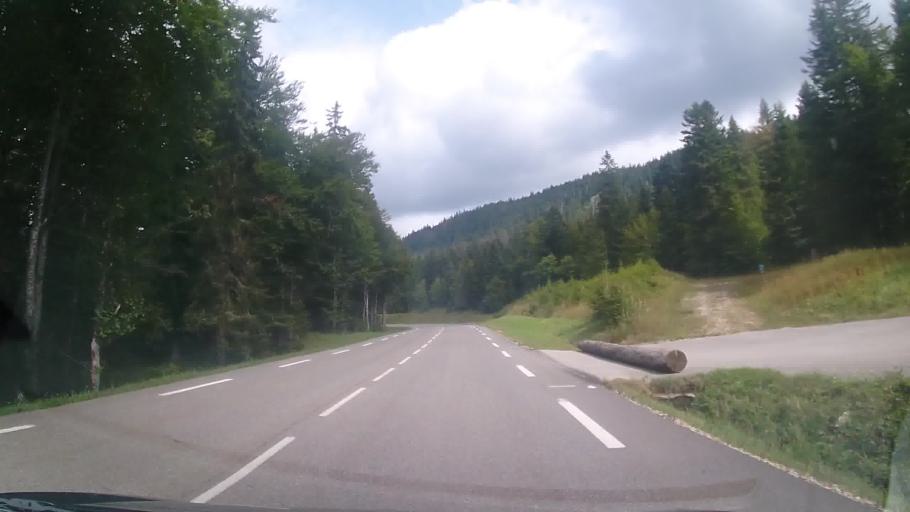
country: FR
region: Rhone-Alpes
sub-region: Departement de l'Ain
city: Gex
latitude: 46.3859
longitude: 6.0496
